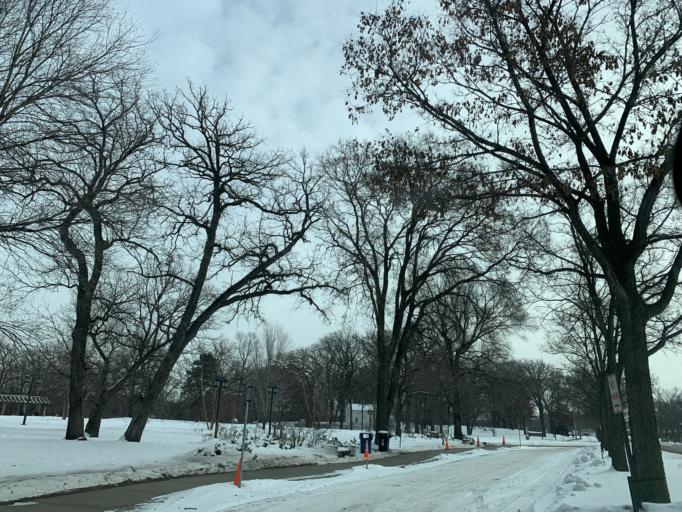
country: US
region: Minnesota
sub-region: Hennepin County
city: Richfield
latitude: 44.9146
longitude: -93.2115
